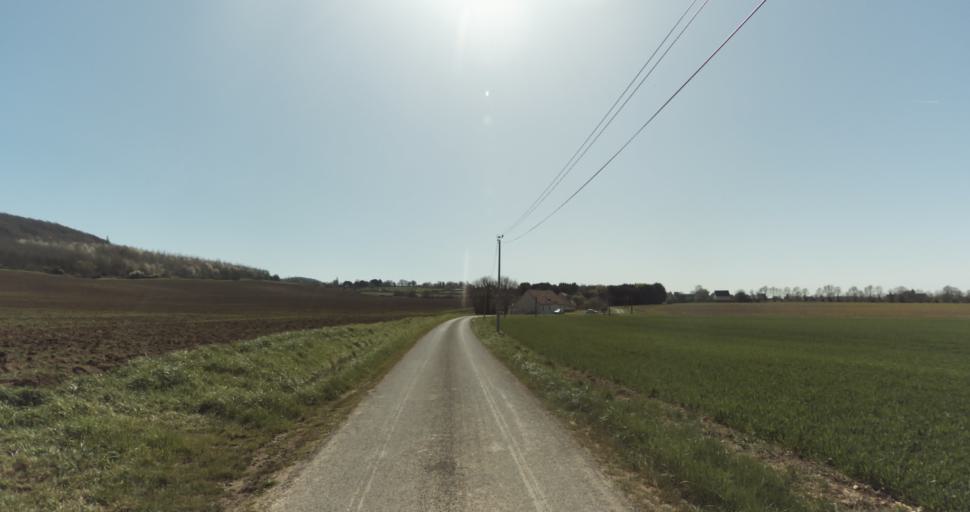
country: FR
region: Lower Normandy
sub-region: Departement du Calvados
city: Saint-Pierre-sur-Dives
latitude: 49.0141
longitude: 0.0297
